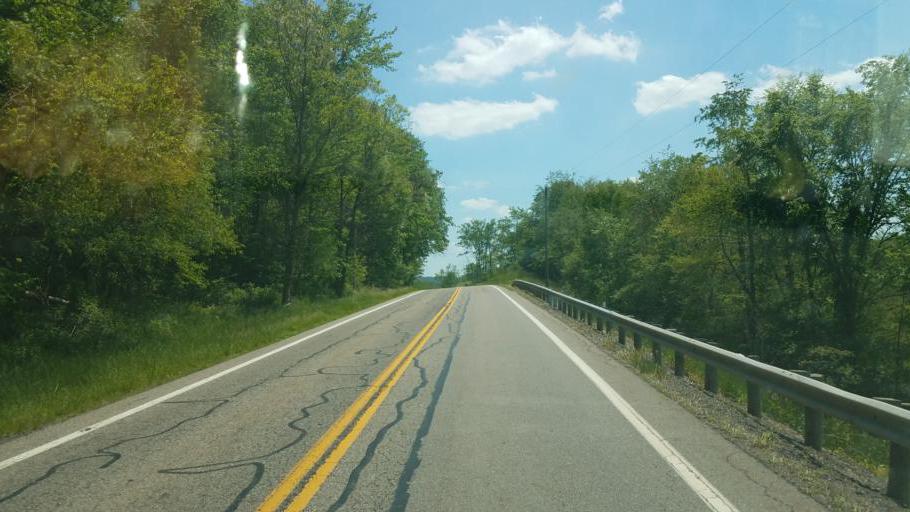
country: US
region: Ohio
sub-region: Muskingum County
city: Frazeysburg
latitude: 40.1475
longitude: -82.2165
